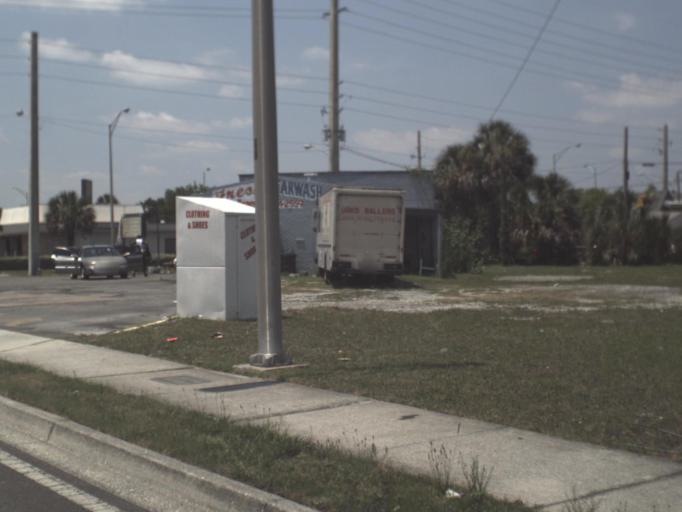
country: US
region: Florida
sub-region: Duval County
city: Jacksonville
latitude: 30.3636
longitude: -81.6638
